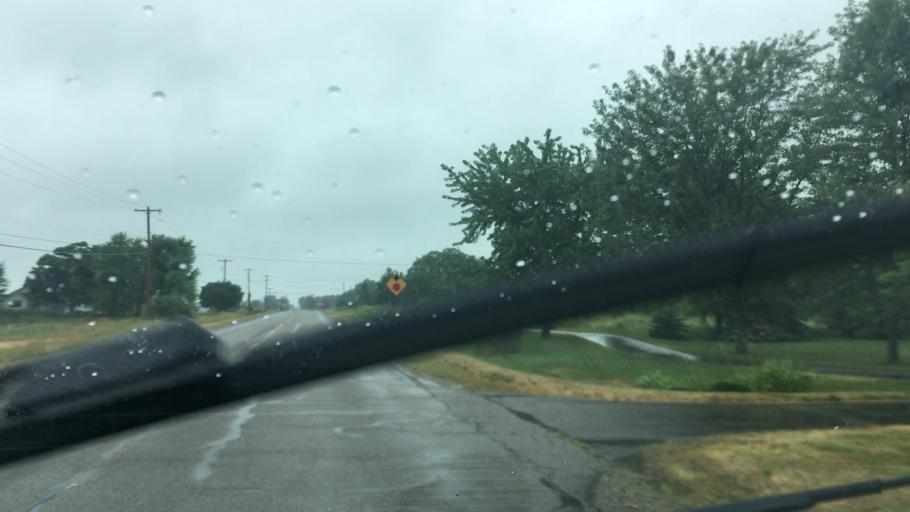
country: US
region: Michigan
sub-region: Ottawa County
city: Hudsonville
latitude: 42.8258
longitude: -85.8583
